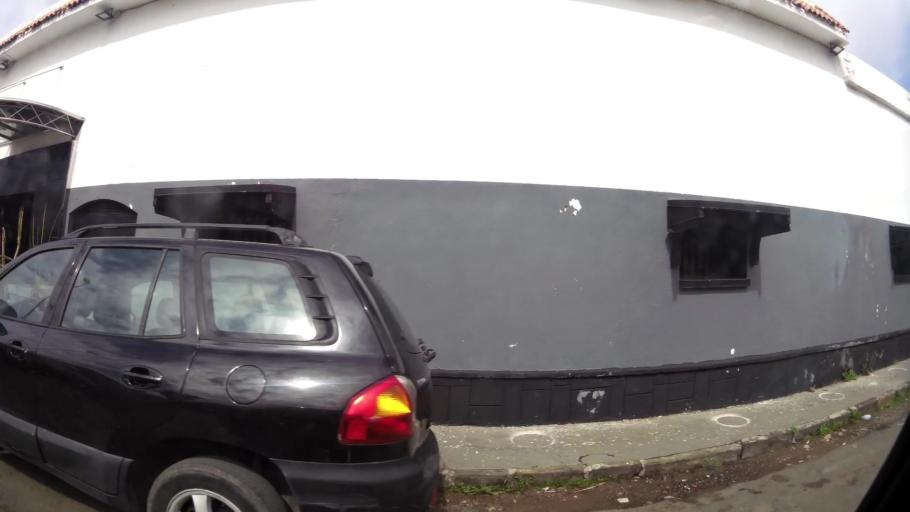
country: MA
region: Grand Casablanca
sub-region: Casablanca
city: Casablanca
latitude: 33.5961
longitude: -7.6726
